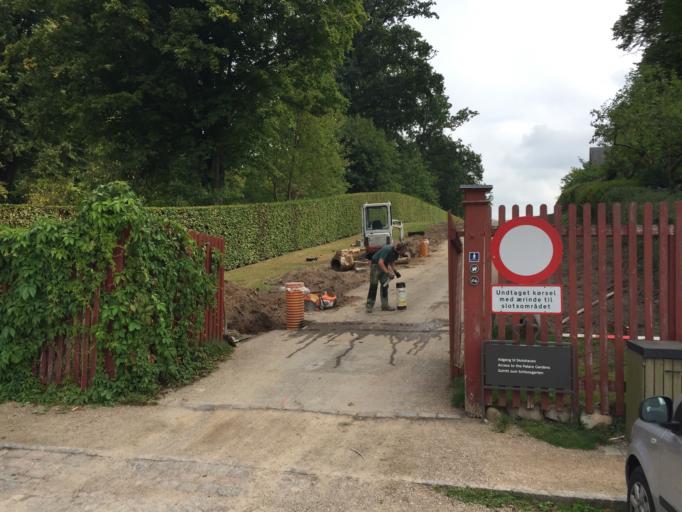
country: DK
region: Capital Region
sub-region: Fredensborg Kommune
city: Fredensborg
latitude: 55.9803
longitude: 12.3962
